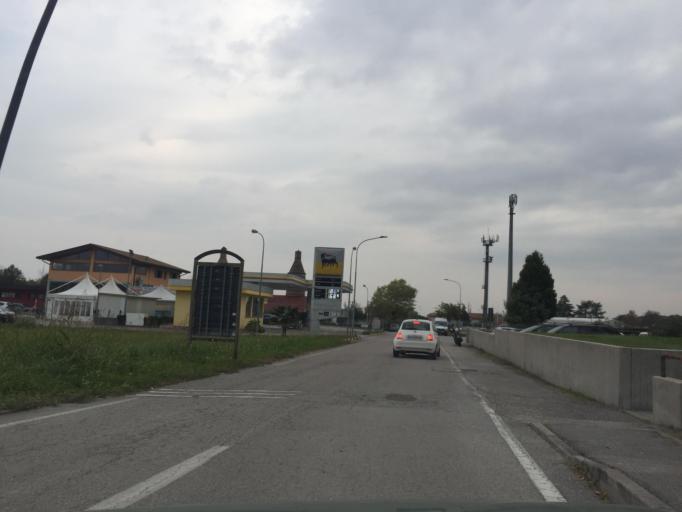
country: IT
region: Friuli Venezia Giulia
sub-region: Provincia di Pordenone
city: Montereale Valcellina
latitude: 46.1525
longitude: 12.6614
